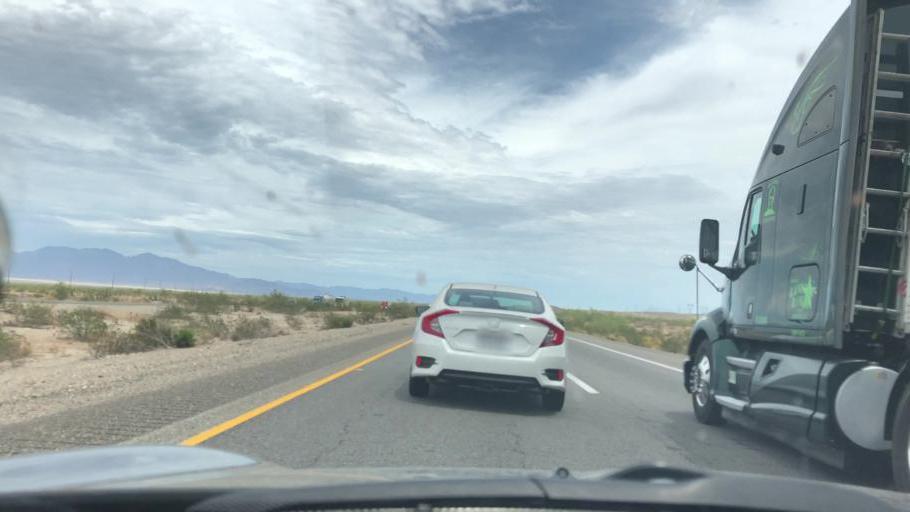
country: US
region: California
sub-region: Imperial County
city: Niland
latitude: 33.7094
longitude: -115.3708
